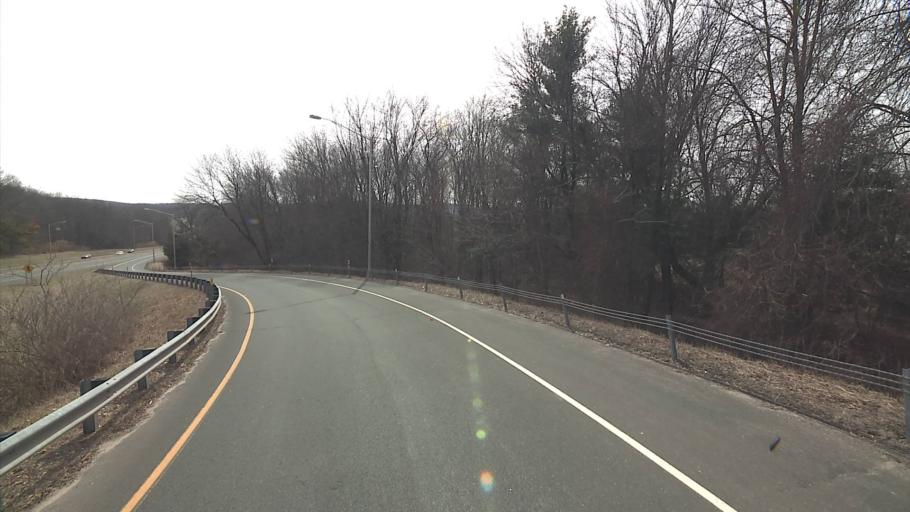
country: US
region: Connecticut
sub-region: Middlesex County
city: Middletown
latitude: 41.5430
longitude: -72.6280
